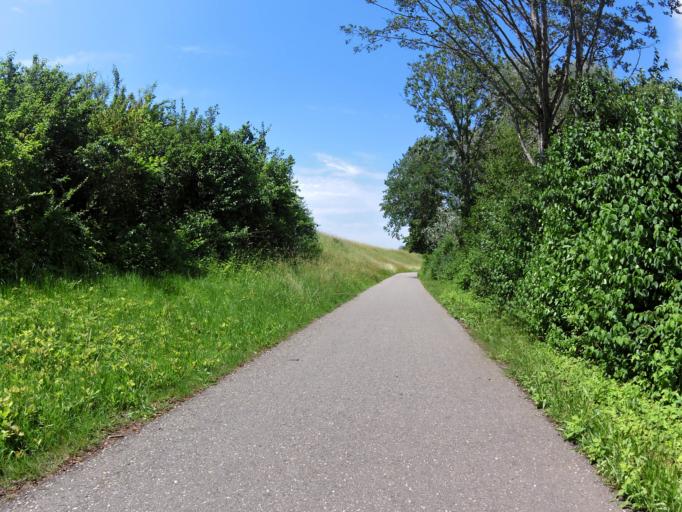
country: DE
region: Baden-Wuerttemberg
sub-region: Freiburg Region
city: Hohberg
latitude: 48.3339
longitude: 7.9142
